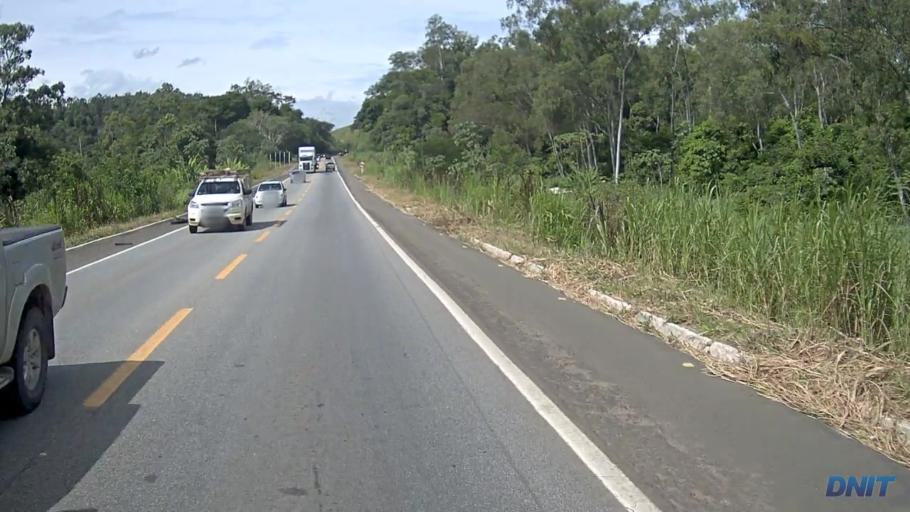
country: BR
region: Minas Gerais
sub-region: Ipatinga
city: Ipatinga
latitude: -19.4287
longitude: -42.5027
